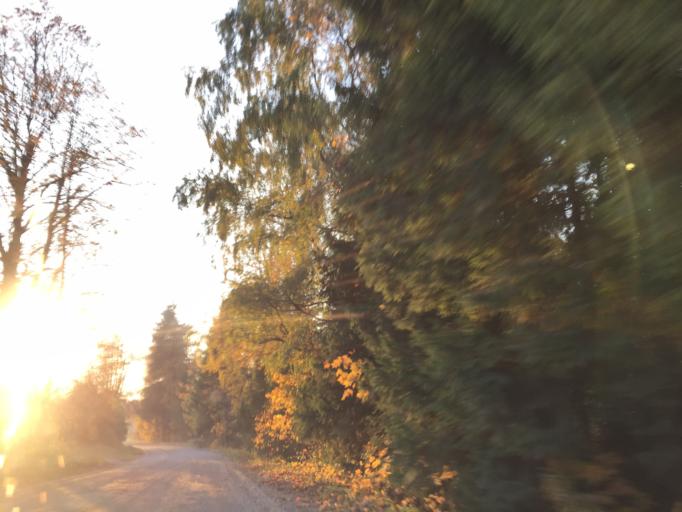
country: LV
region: Priekule
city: Priekule
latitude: 56.4805
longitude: 21.7283
